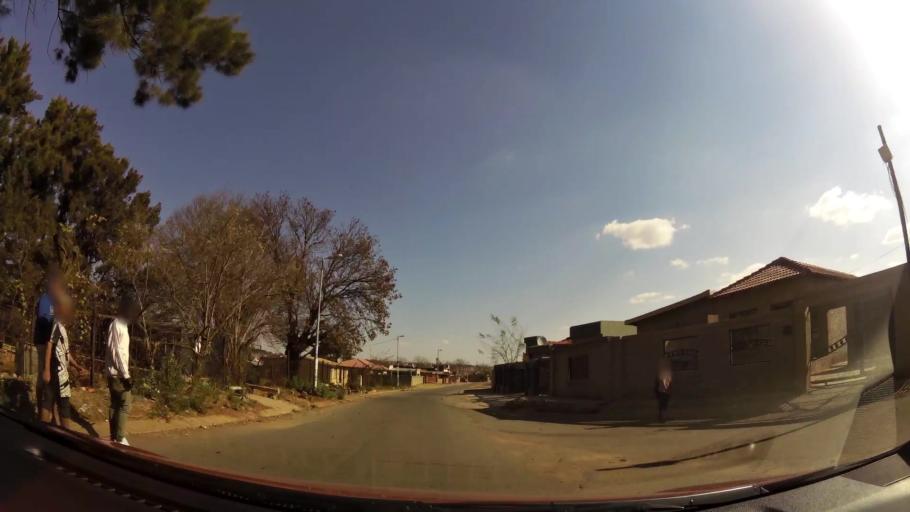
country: ZA
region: Gauteng
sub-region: City of Johannesburg Metropolitan Municipality
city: Soweto
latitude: -26.2359
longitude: 27.8804
